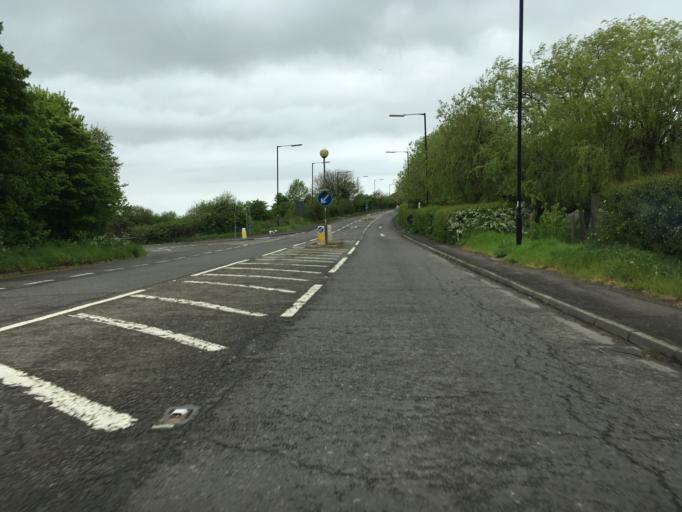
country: GB
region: England
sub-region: North Somerset
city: Banwell
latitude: 51.3311
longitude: -2.8958
